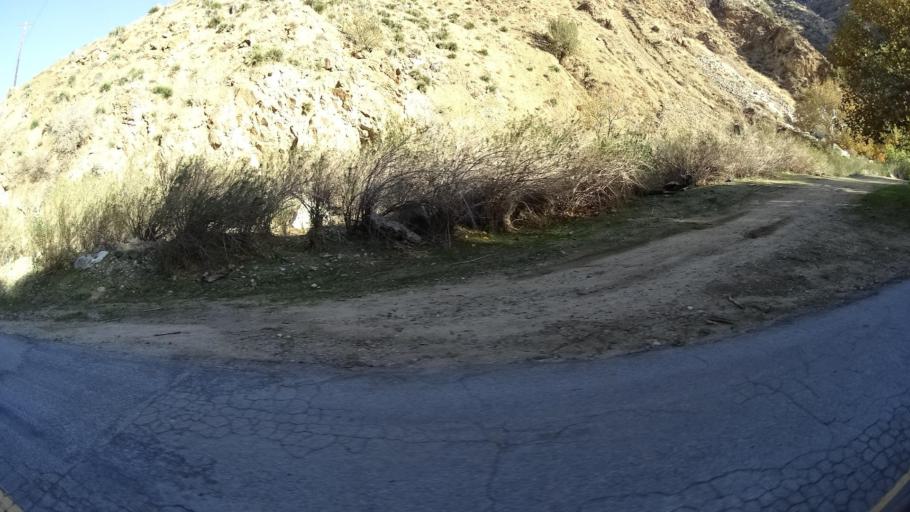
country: US
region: California
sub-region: Kern County
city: Golden Hills
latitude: 35.3108
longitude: -118.5008
